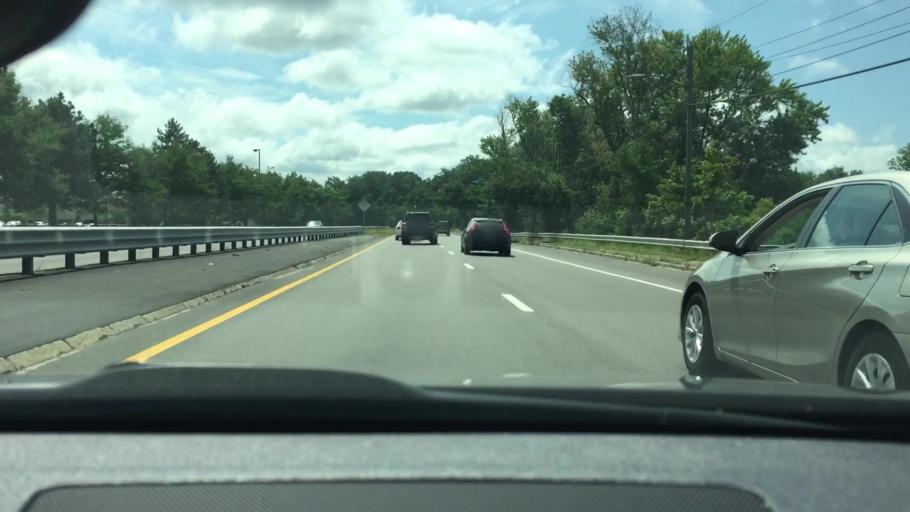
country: US
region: Massachusetts
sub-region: Norfolk County
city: Dedham
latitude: 42.2541
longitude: -71.1714
